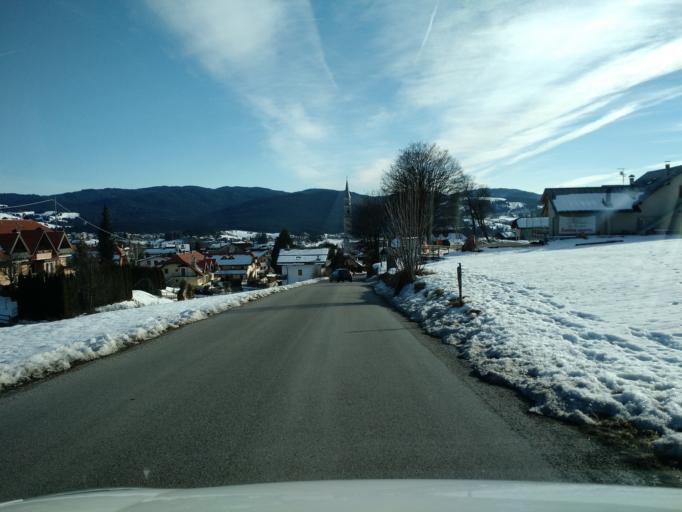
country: IT
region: Veneto
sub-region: Provincia di Vicenza
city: Roana
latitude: 45.8794
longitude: 11.4623
